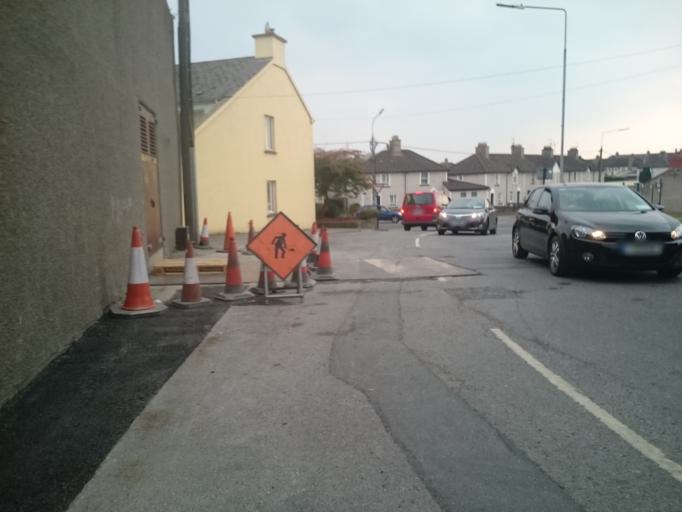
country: IE
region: Leinster
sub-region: Kilkenny
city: Kilkenny
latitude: 52.6569
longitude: -7.2601
